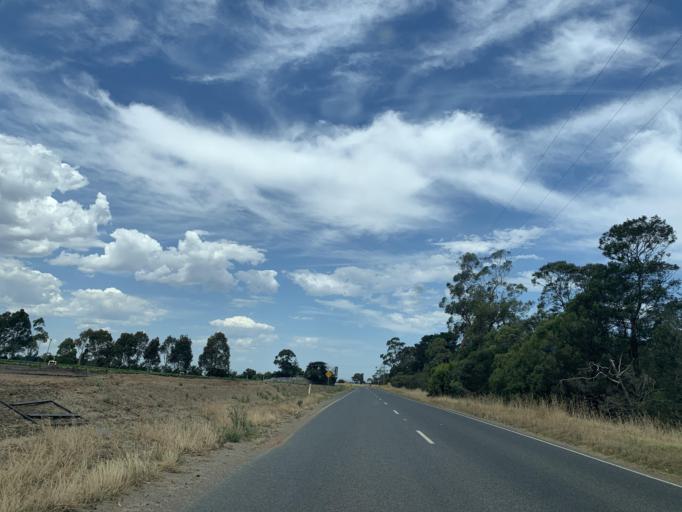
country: AU
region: Victoria
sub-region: Casey
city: Junction Village
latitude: -38.1328
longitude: 145.3321
